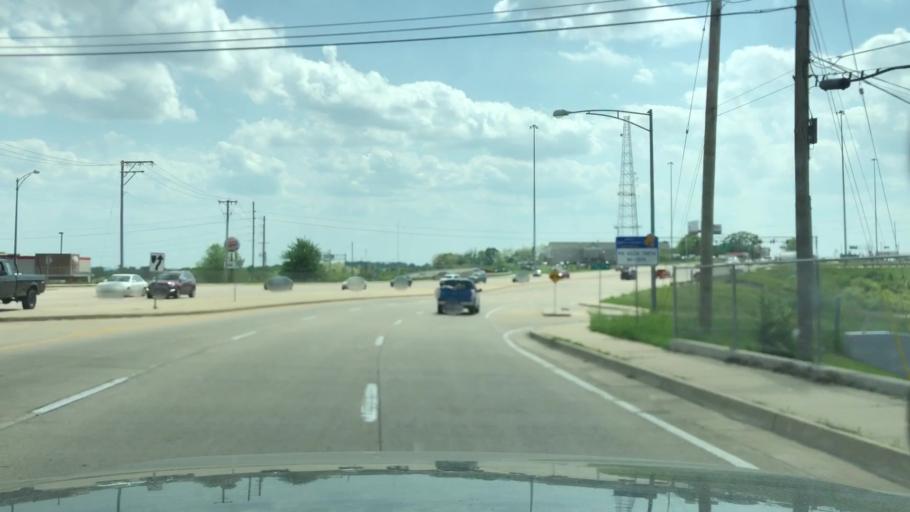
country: US
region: Missouri
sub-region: Saint Charles County
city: Saint Charles
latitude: 38.7785
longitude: -90.5094
